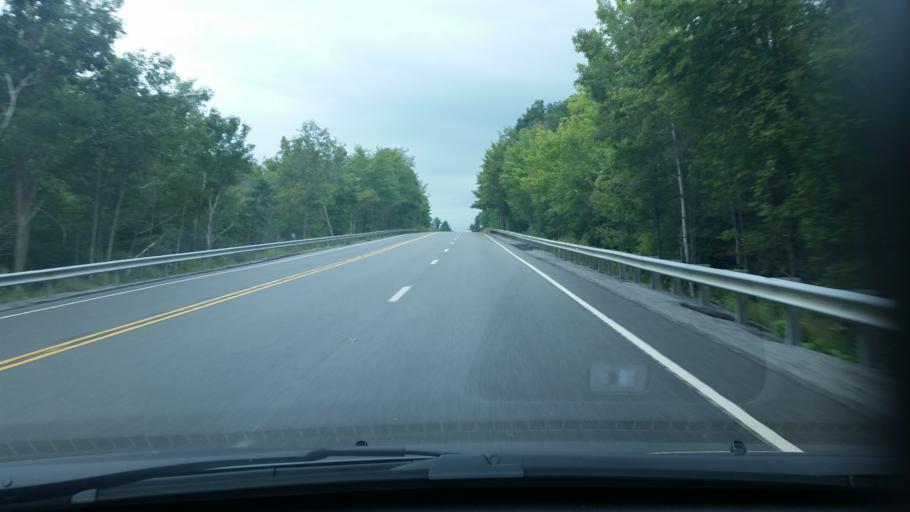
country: US
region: Pennsylvania
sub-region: Clearfield County
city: Shiloh
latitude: 41.0739
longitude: -78.3072
